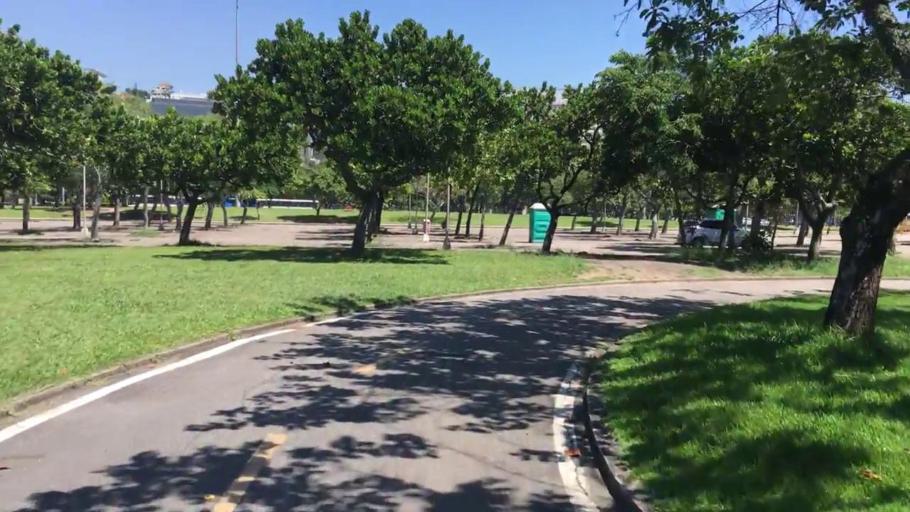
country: BR
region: Rio de Janeiro
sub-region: Rio De Janeiro
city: Rio de Janeiro
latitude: -22.9180
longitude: -43.1733
